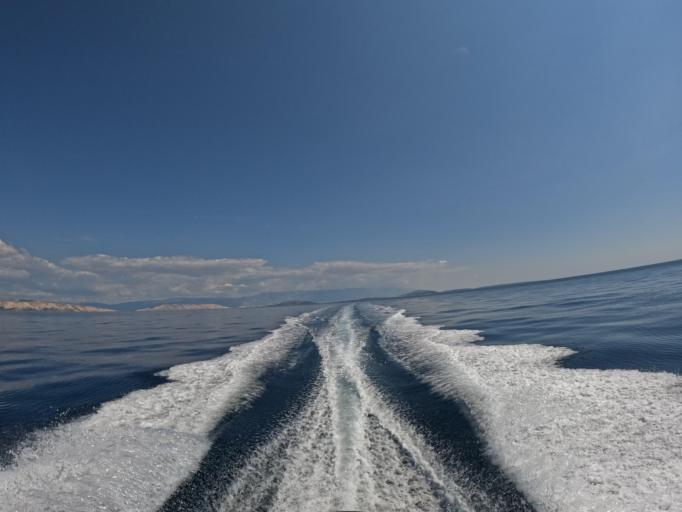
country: HR
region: Primorsko-Goranska
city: Punat
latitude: 44.9136
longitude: 14.5837
